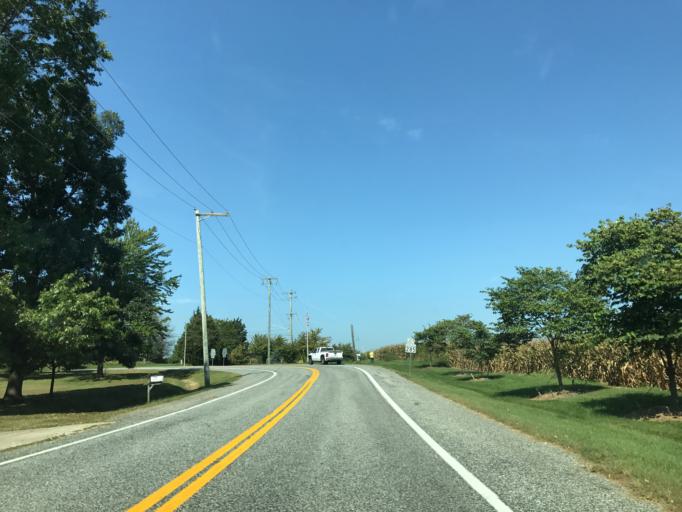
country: US
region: Maryland
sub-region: Cecil County
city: Elkton
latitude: 39.5325
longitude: -75.8070
